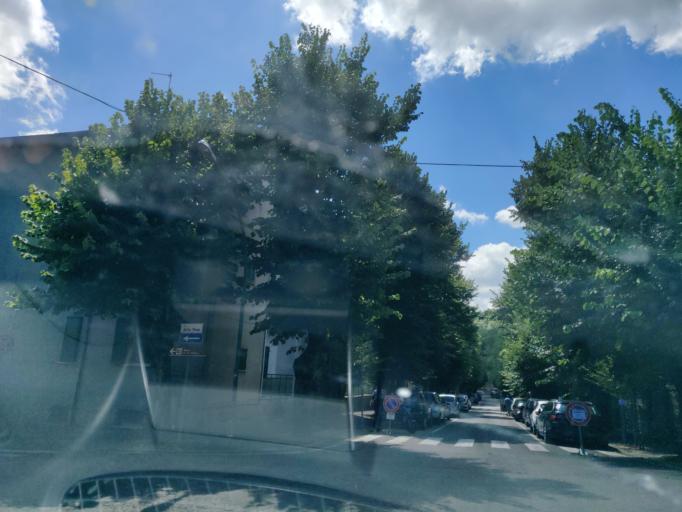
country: IT
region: Tuscany
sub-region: Provincia di Siena
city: Abbadia San Salvatore
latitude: 42.8814
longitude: 11.6712
